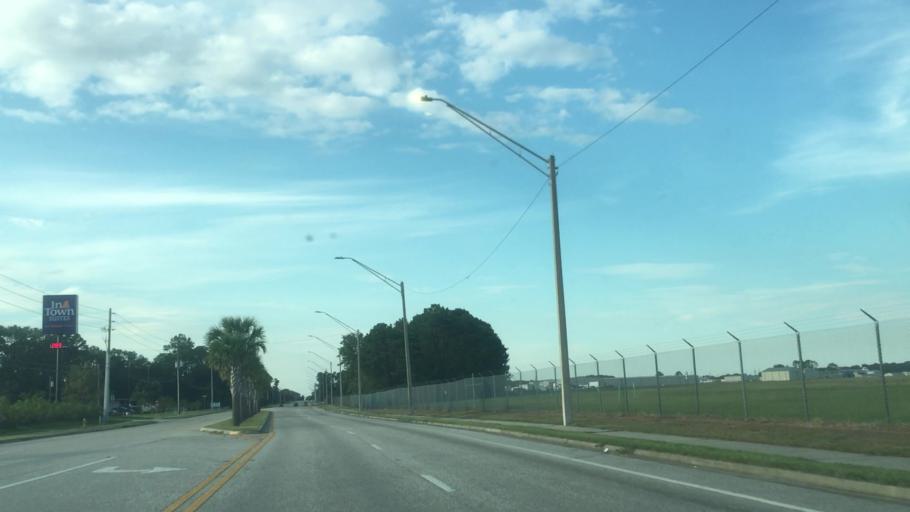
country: US
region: Florida
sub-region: Duval County
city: Atlantic Beach
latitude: 30.3256
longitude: -81.5231
